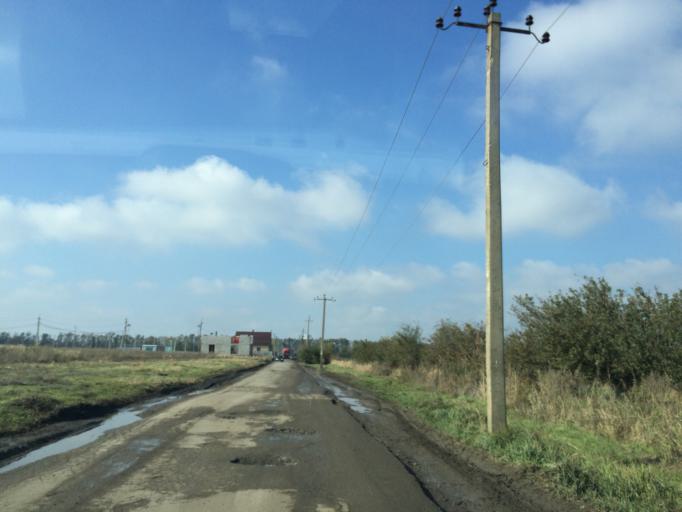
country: RU
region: Rostov
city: Aksay
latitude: 47.2919
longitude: 39.8390
